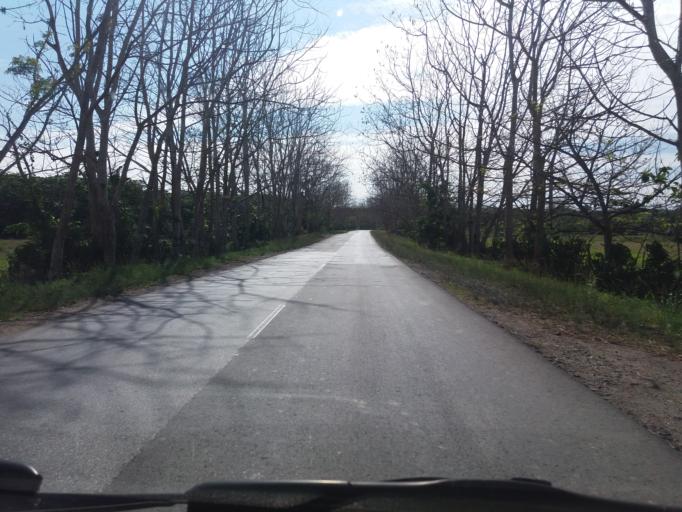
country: CU
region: Cienfuegos
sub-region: Municipio de Cienfuegos
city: Cienfuegos
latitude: 22.1654
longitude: -80.3719
